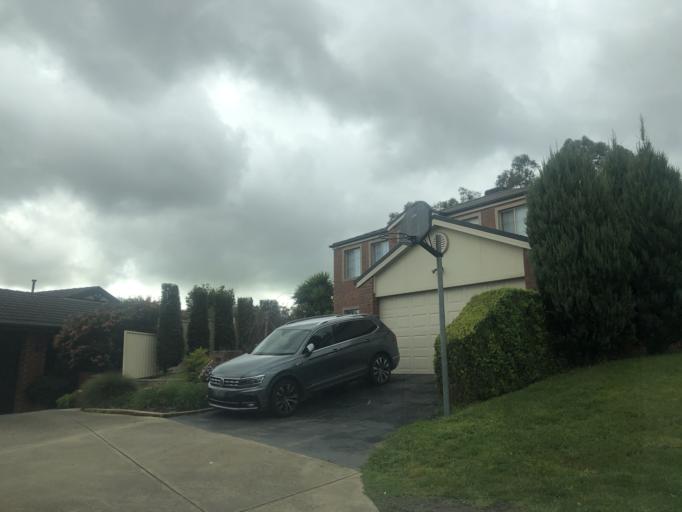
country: AU
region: Victoria
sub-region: Knox
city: Rowville
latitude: -37.9373
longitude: 145.2545
